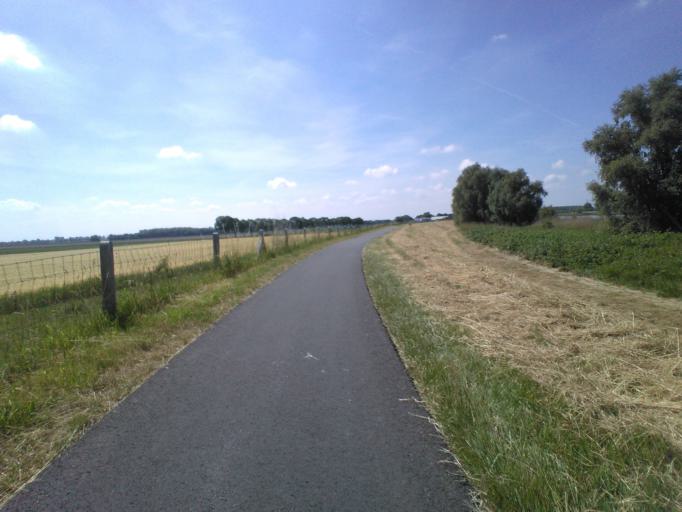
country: NL
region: North Brabant
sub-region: Gemeente Werkendam
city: Werkendam
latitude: 51.7887
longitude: 4.8774
